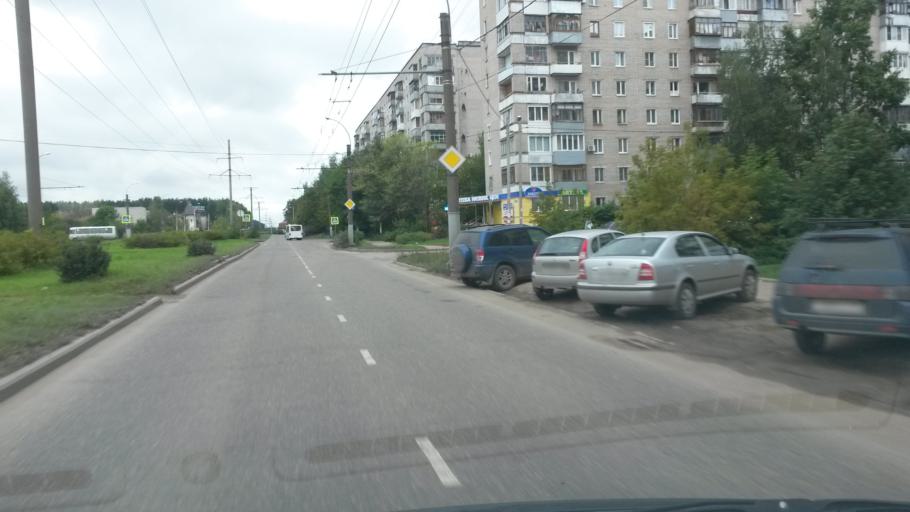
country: RU
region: Ivanovo
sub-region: Gorod Ivanovo
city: Ivanovo
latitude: 56.9598
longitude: 41.0270
